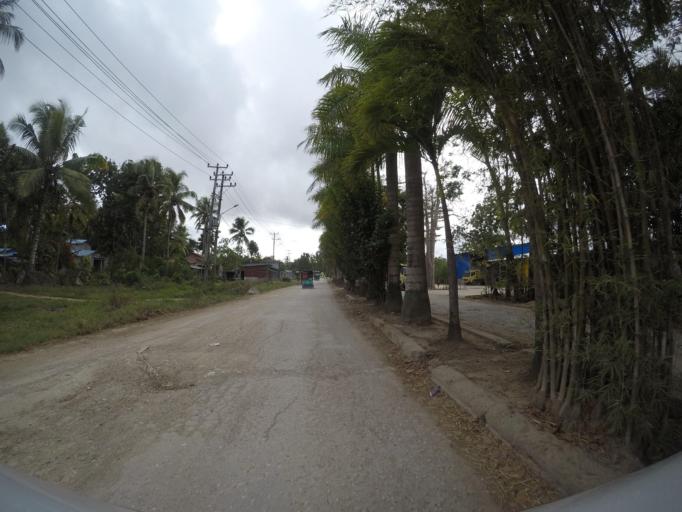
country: TL
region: Lautem
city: Lospalos
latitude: -8.5141
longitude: 127.0030
